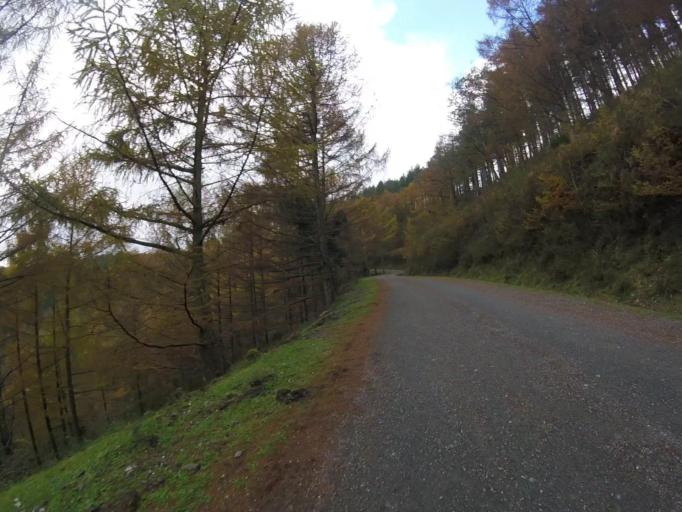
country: ES
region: Navarre
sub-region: Provincia de Navarra
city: Goizueta
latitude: 43.2129
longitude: -1.8237
